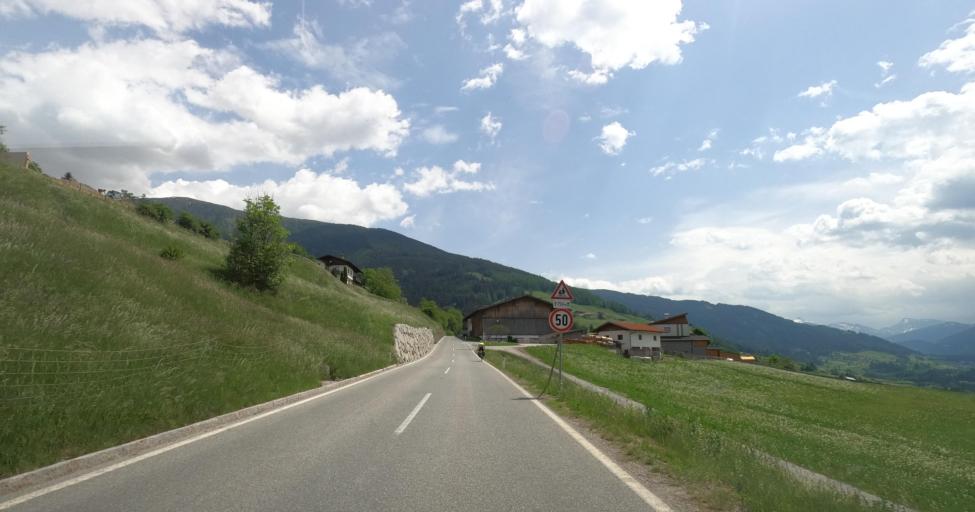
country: AT
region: Tyrol
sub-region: Politischer Bezirk Innsbruck Land
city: Ellbogen
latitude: 47.1656
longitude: 11.4484
